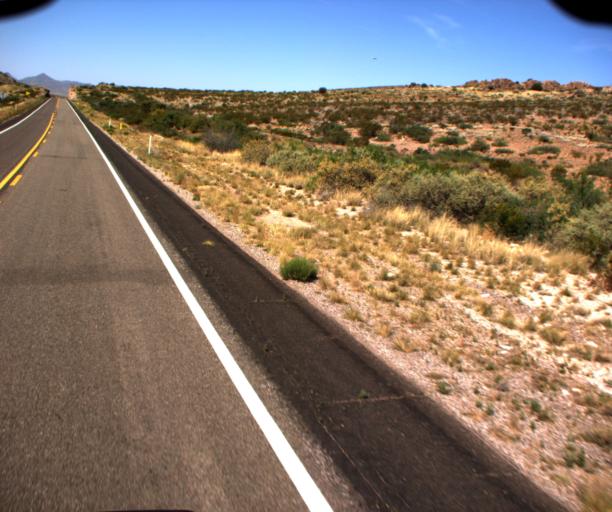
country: US
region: Arizona
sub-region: Greenlee County
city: Clifton
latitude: 32.7726
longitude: -109.3124
